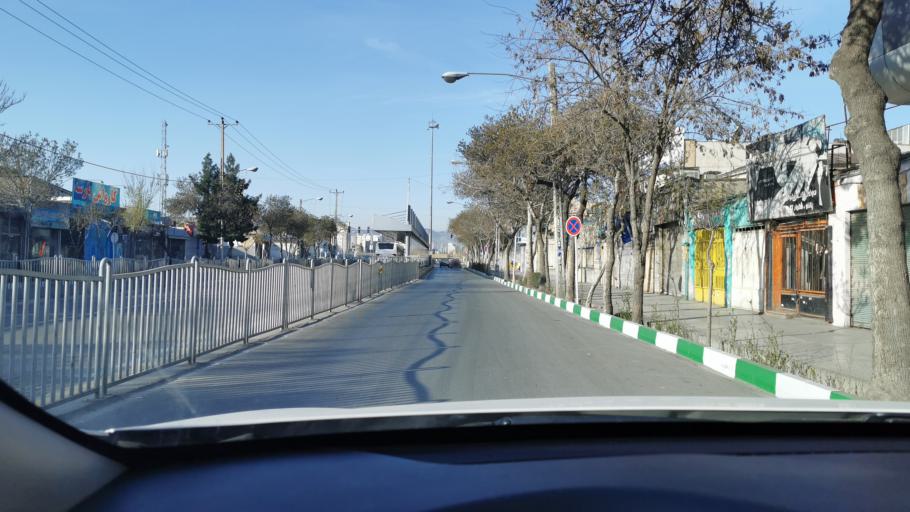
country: IR
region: Razavi Khorasan
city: Mashhad
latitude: 36.3000
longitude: 59.6347
